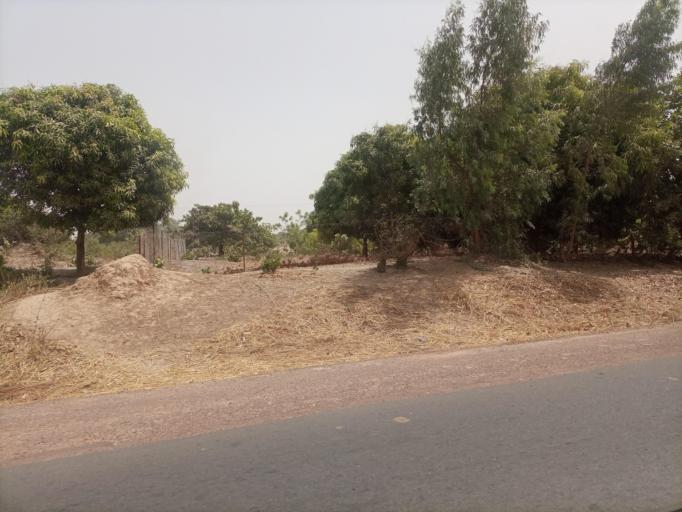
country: SN
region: Fatick
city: Sokone
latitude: 13.7350
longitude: -16.4236
